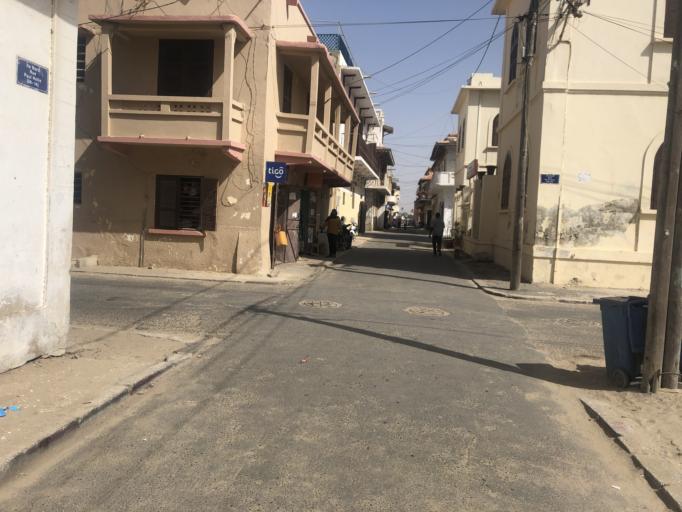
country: SN
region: Saint-Louis
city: Saint-Louis
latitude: 16.0283
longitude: -16.5051
